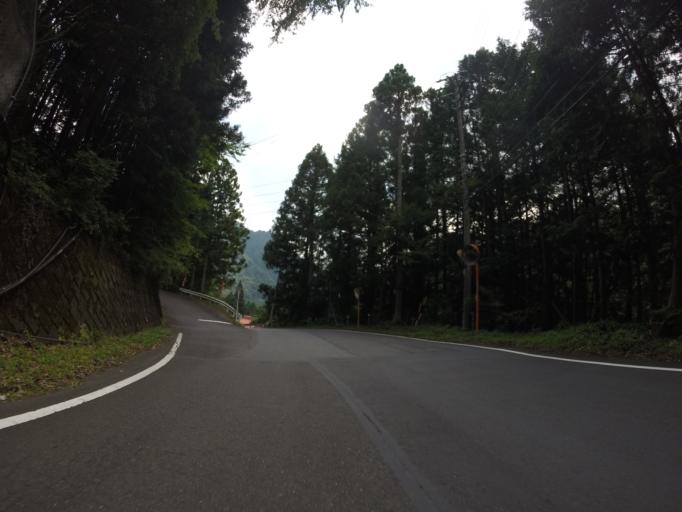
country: JP
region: Shizuoka
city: Fujinomiya
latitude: 35.2687
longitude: 138.3264
